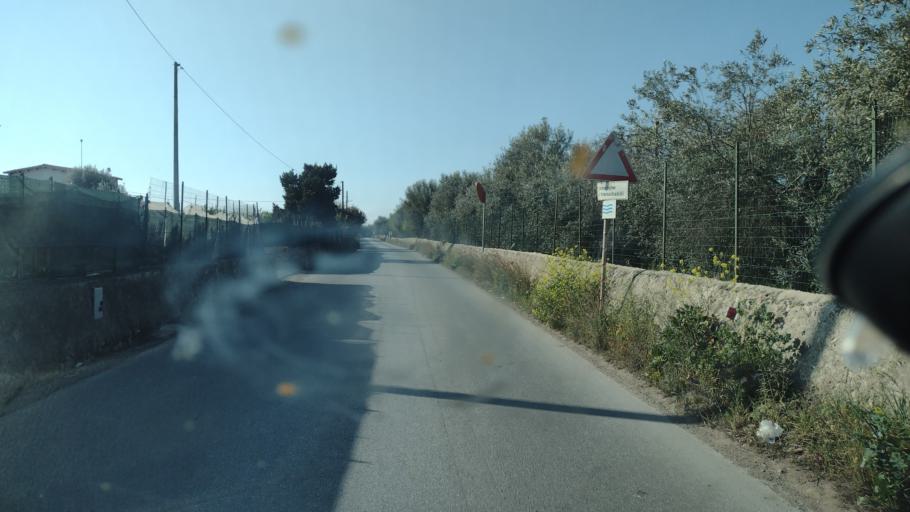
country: IT
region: Sicily
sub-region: Provincia di Siracusa
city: Avola
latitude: 36.8865
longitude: 15.1310
